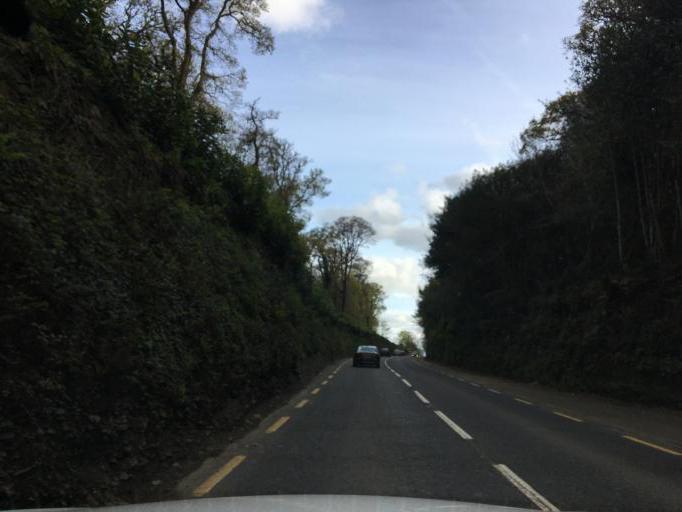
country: IE
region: Leinster
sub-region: Loch Garman
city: New Ross
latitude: 52.4176
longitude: -6.9365
